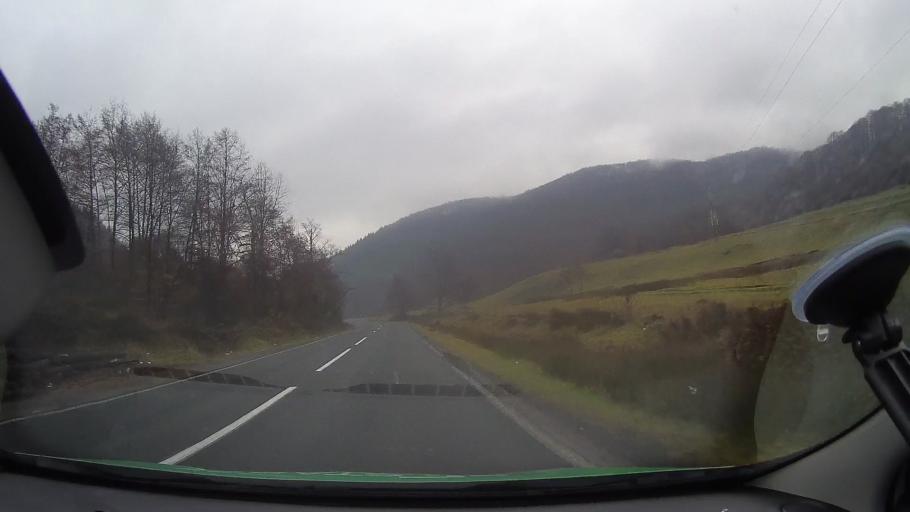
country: RO
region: Arad
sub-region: Comuna Plescuta
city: Plescuta
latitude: 46.2988
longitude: 22.4535
